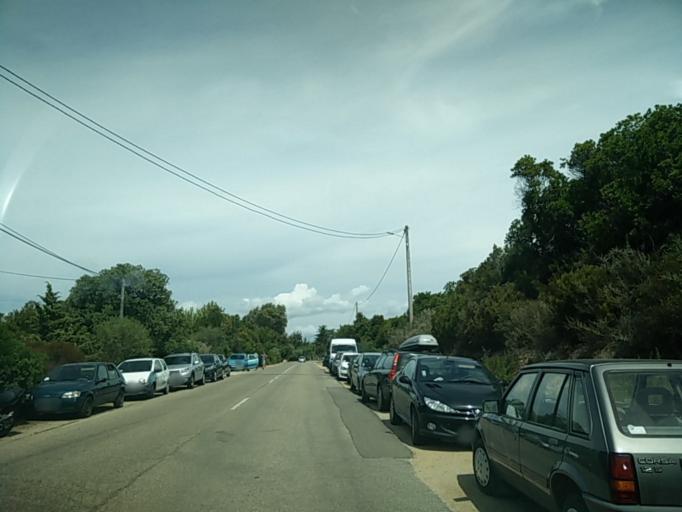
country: FR
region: Corsica
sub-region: Departement de la Corse-du-Sud
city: Pietrosella
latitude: 41.8154
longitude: 8.7744
